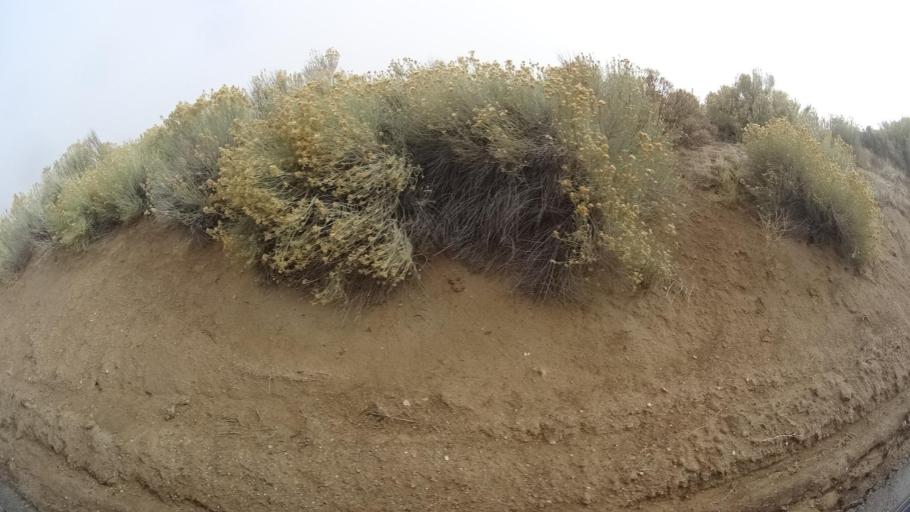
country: US
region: California
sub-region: Kern County
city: Maricopa
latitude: 34.9324
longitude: -119.4137
